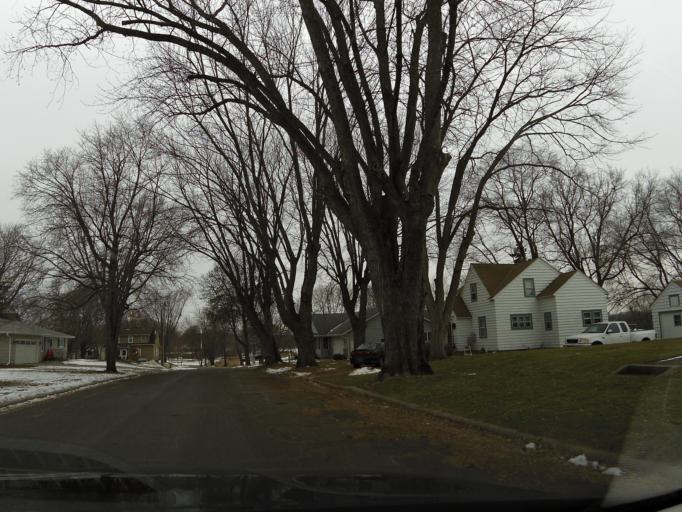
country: US
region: Minnesota
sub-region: Carver County
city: Cologne
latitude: 44.7725
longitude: -93.7799
